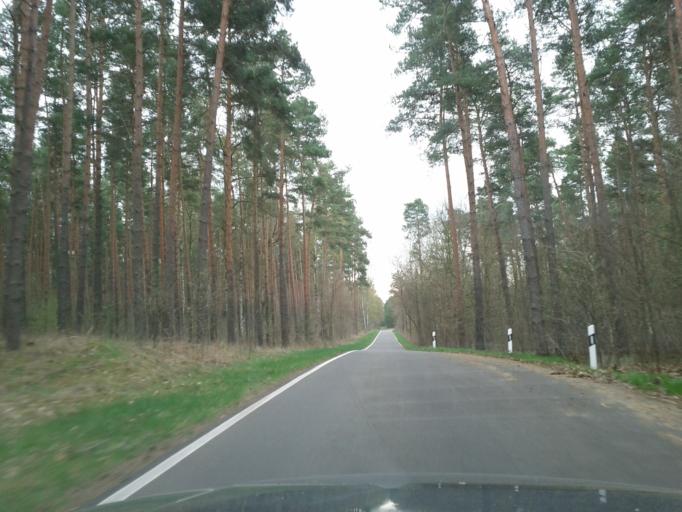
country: DE
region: Brandenburg
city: Spreenhagen
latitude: 52.3852
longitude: 13.8525
